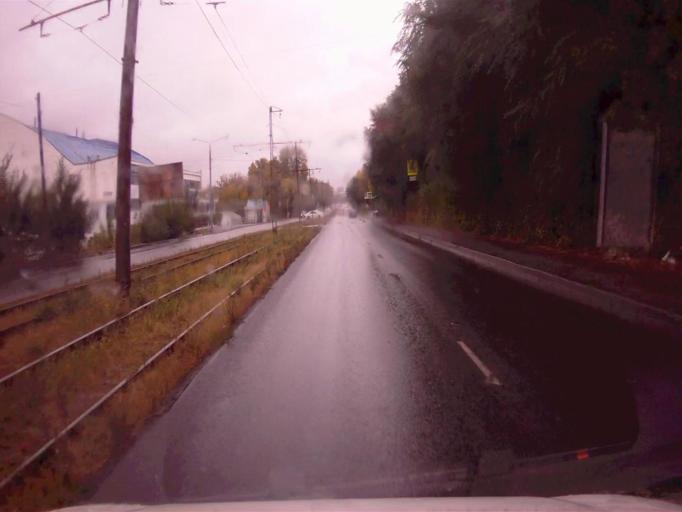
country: RU
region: Chelyabinsk
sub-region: Gorod Chelyabinsk
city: Chelyabinsk
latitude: 55.1768
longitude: 61.4149
